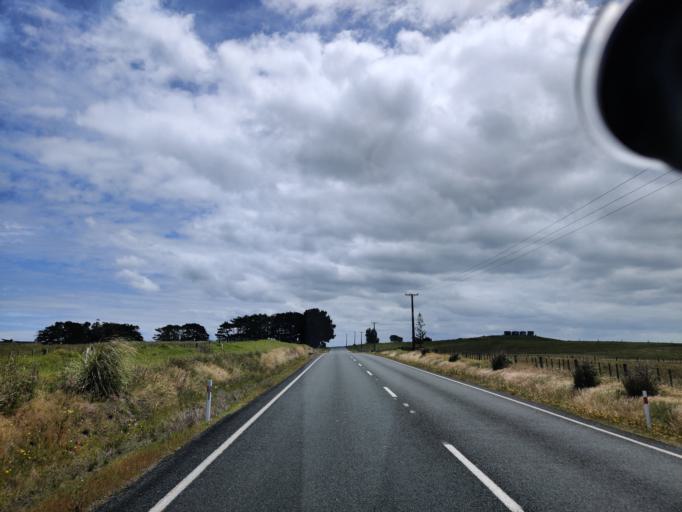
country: NZ
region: Northland
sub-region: Far North District
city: Kaitaia
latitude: -34.6966
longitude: 173.0250
